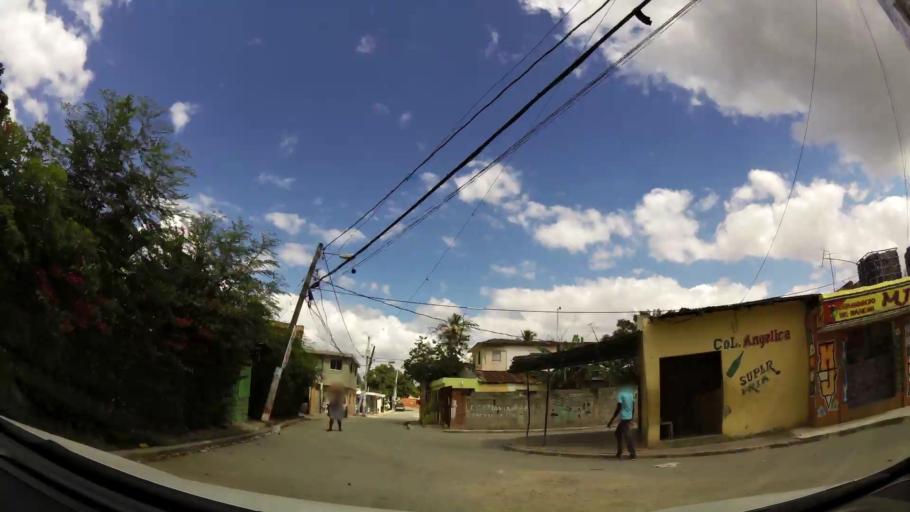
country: DO
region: Nacional
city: Ensanche Luperon
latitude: 18.5301
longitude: -69.9115
